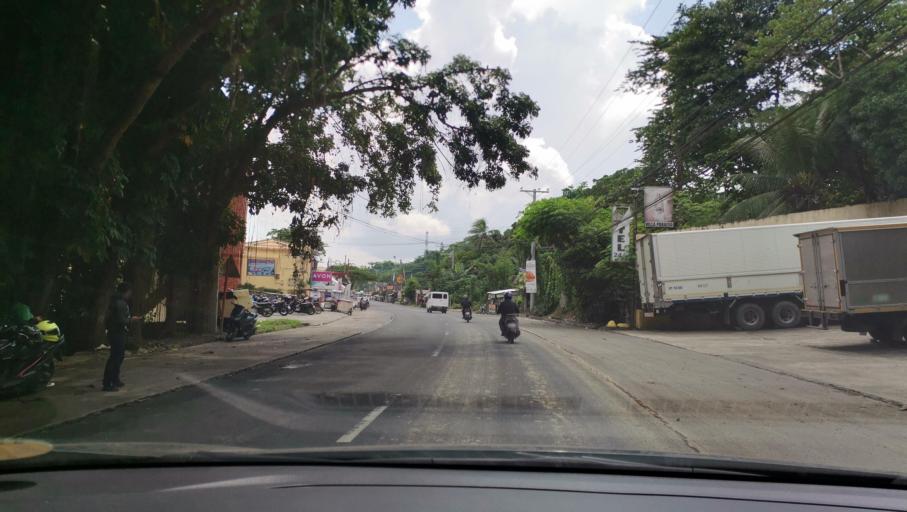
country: PH
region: Calabarzon
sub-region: Province of Quezon
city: Calauag
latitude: 13.9531
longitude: 122.2942
